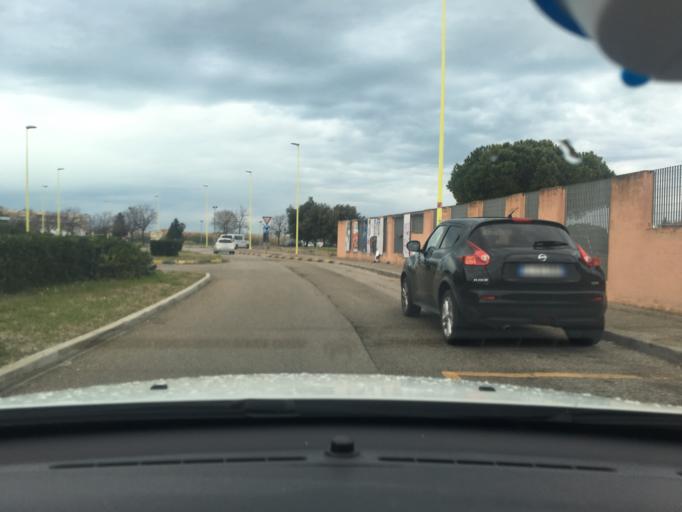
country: IT
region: Molise
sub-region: Provincia di Campobasso
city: Termoli
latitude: 41.9715
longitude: 14.9937
